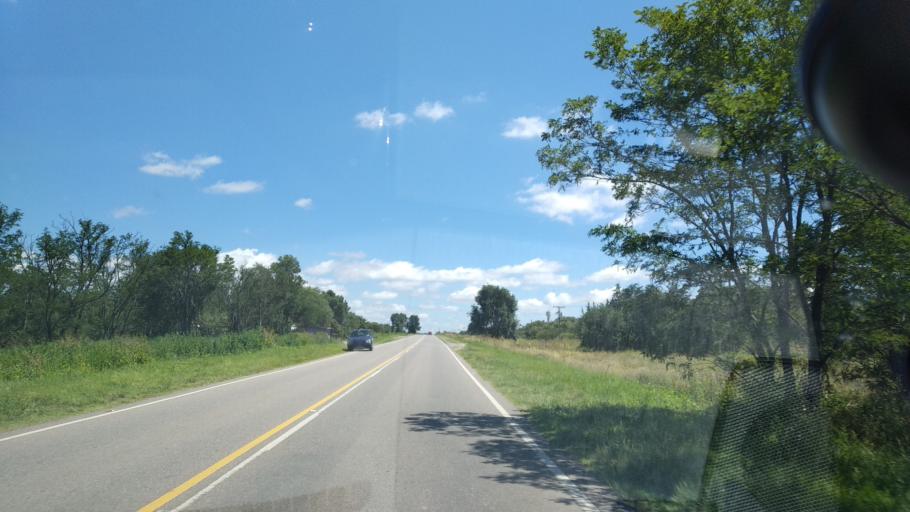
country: AR
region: Cordoba
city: Salsacate
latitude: -31.4913
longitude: -65.1077
